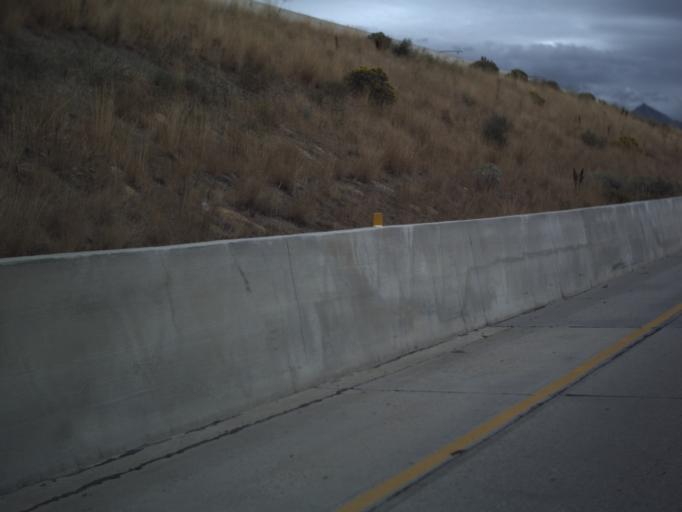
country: US
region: Utah
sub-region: Utah County
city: Lehi
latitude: 40.4313
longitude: -111.8804
